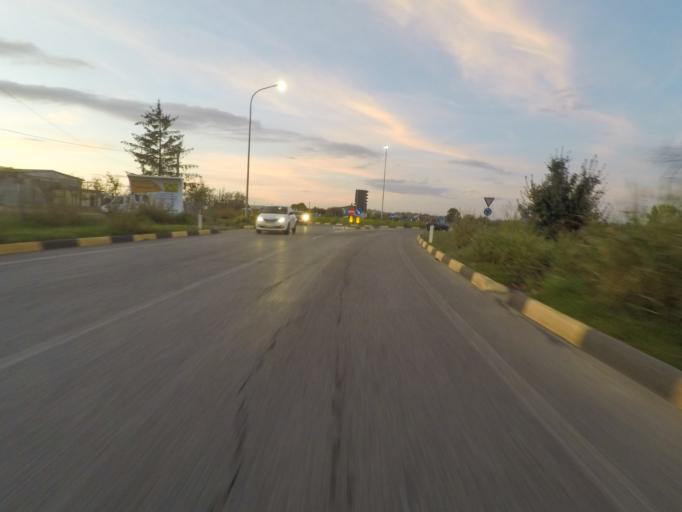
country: IT
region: Tuscany
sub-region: Provincia di Siena
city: Sinalunga
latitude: 43.2232
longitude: 11.7534
